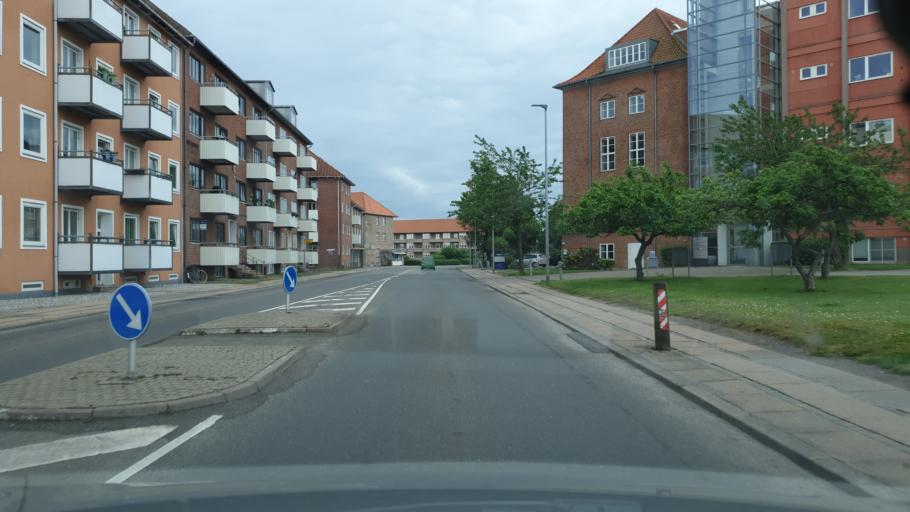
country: DK
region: South Denmark
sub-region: Kolding Kommune
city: Kolding
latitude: 55.4846
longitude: 9.4802
